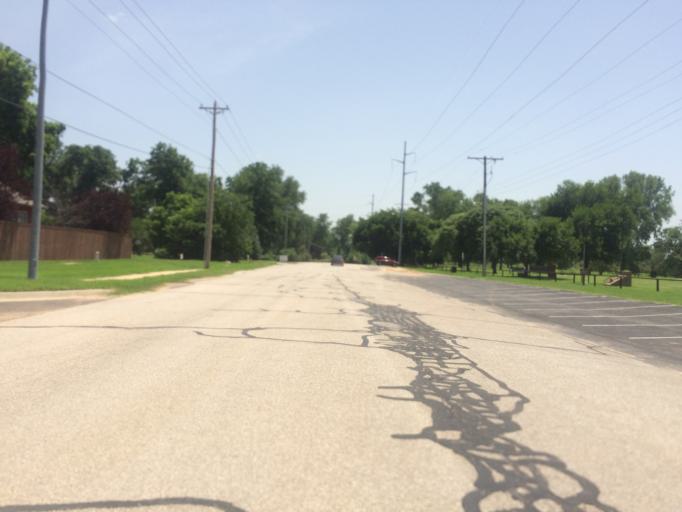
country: US
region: Oklahoma
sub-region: Cleveland County
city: Norman
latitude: 35.1926
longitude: -97.4768
